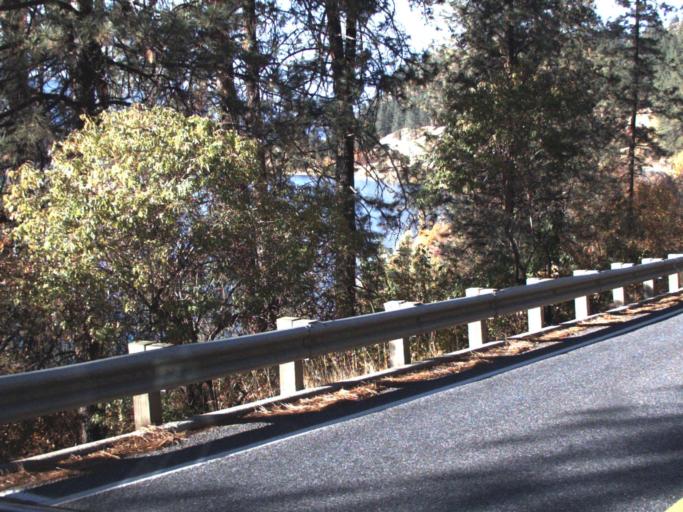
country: US
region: Washington
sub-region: Stevens County
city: Kettle Falls
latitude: 48.6255
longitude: -118.0723
